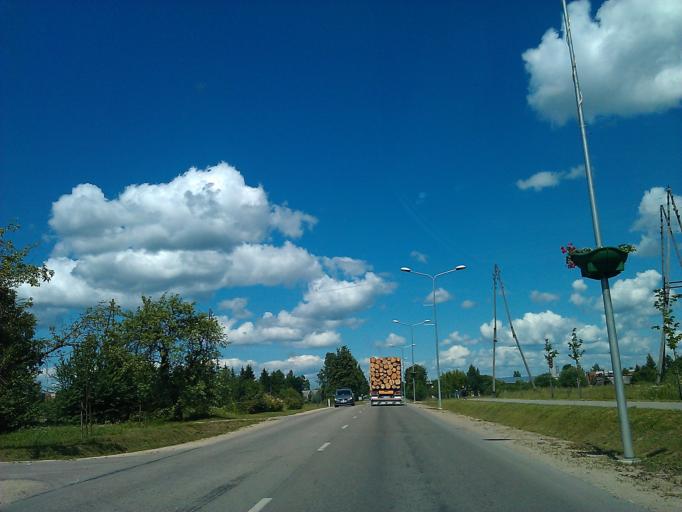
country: LV
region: Vilanu
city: Vilani
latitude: 56.5620
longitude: 26.9270
